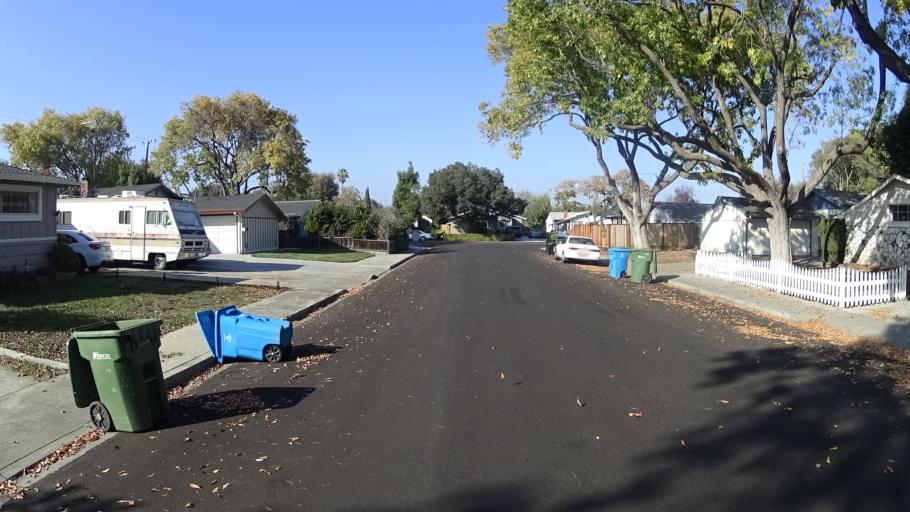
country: US
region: California
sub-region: Santa Clara County
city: Santa Clara
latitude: 37.3612
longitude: -121.9848
